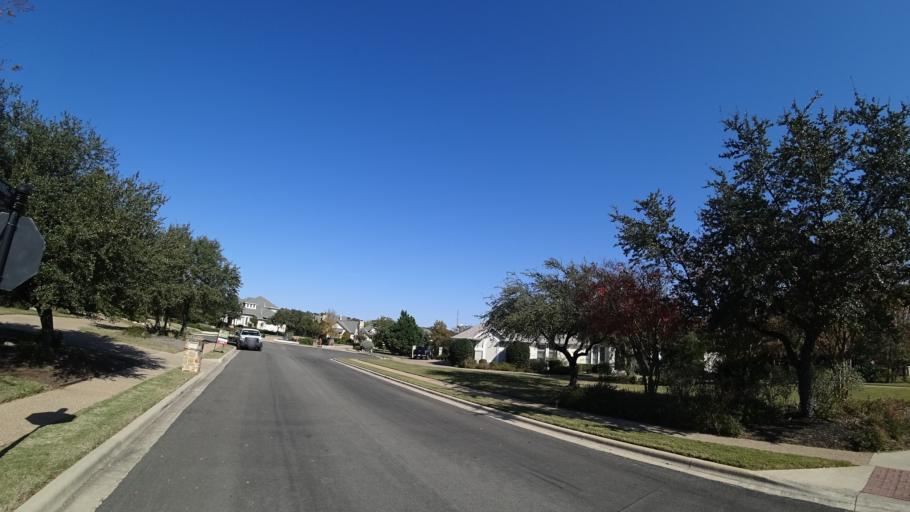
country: US
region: Texas
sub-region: Williamson County
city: Anderson Mill
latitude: 30.3815
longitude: -97.8505
